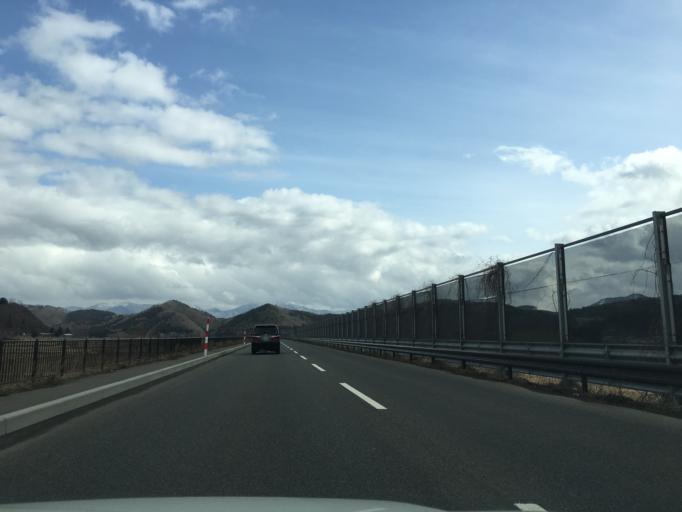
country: JP
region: Akita
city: Hanawa
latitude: 40.2300
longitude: 140.7068
